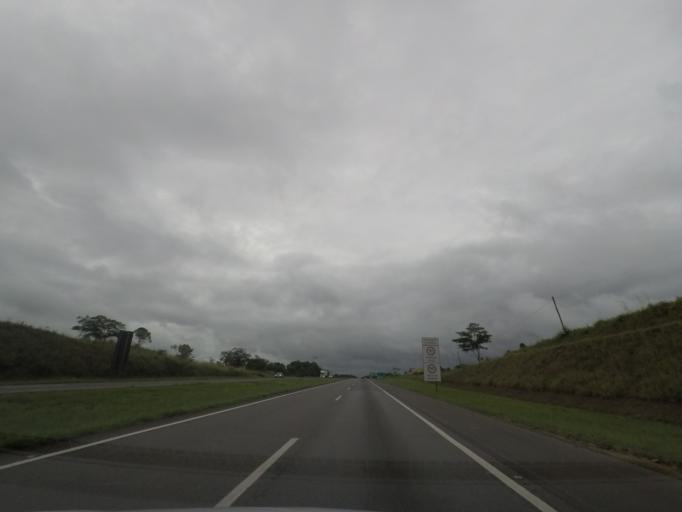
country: BR
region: Sao Paulo
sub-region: Pariquera-Acu
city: Pariquera Acu
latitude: -24.6366
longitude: -47.9104
